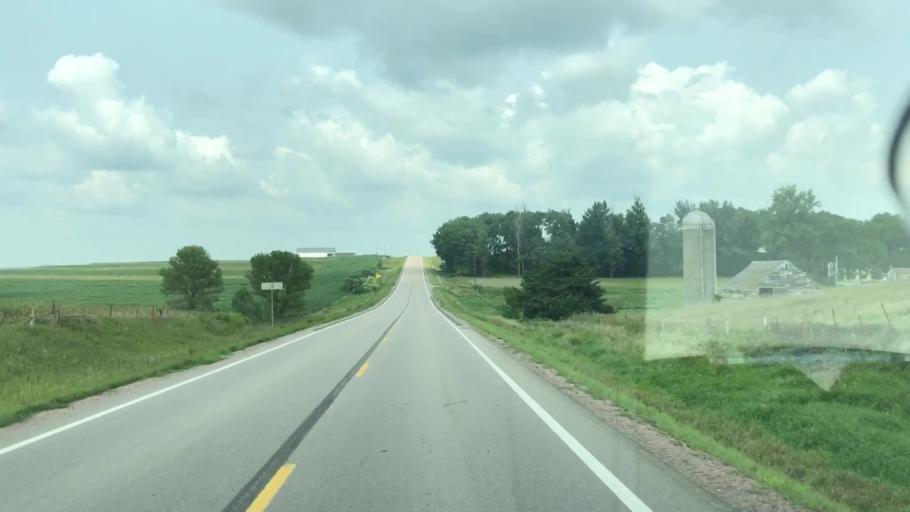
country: US
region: Iowa
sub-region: Plymouth County
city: Kingsley
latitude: 42.5969
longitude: -95.9572
